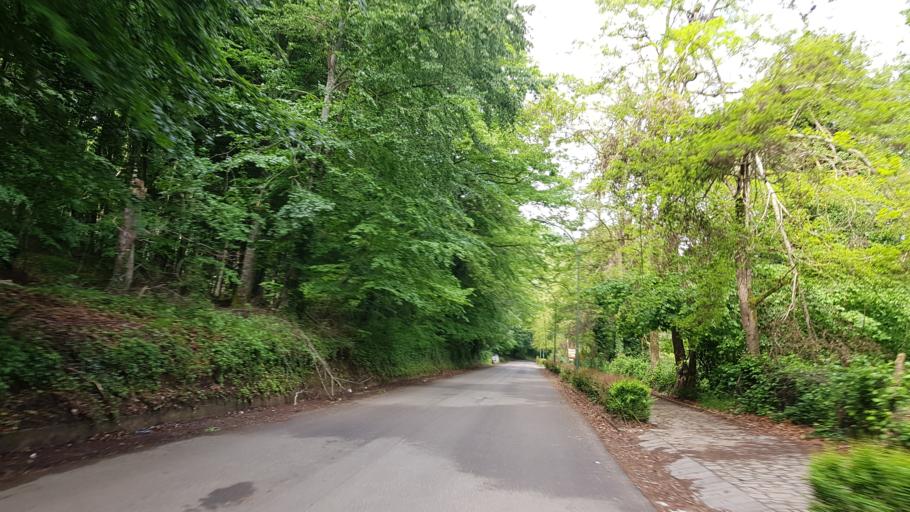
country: IT
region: Basilicate
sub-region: Provincia di Potenza
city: Rionero in Vulture
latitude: 40.9266
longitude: 15.6090
